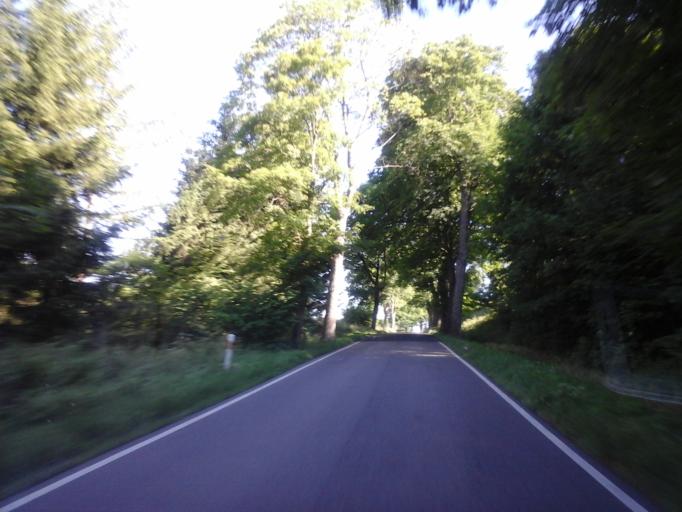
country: PL
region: West Pomeranian Voivodeship
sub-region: Powiat drawski
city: Zlocieniec
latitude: 53.6172
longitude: 15.9228
